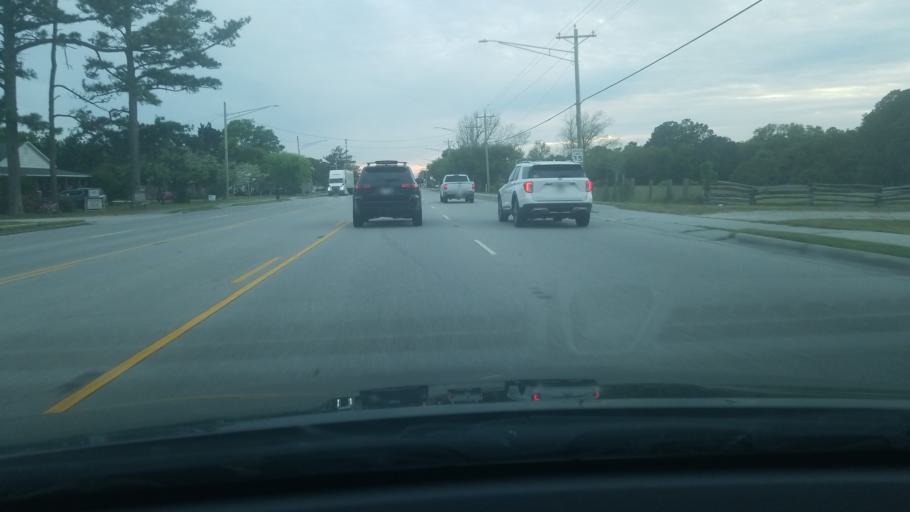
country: US
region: North Carolina
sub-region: Carteret County
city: Cedar Point
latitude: 34.6820
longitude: -77.0866
